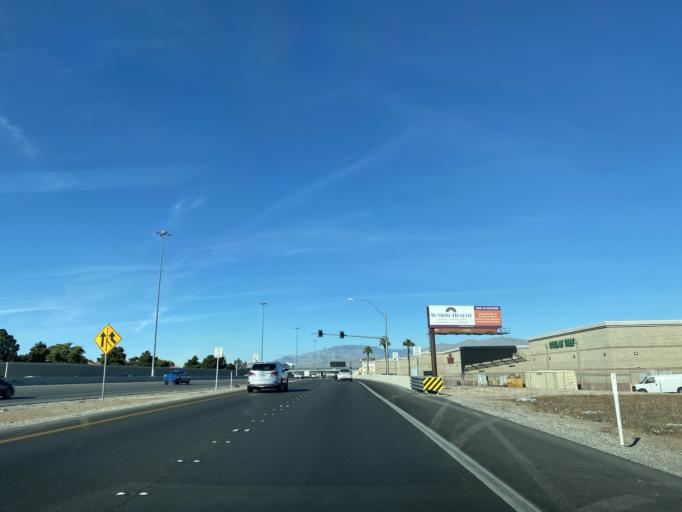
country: US
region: Nevada
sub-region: Clark County
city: Spring Valley
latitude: 36.1985
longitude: -115.2435
